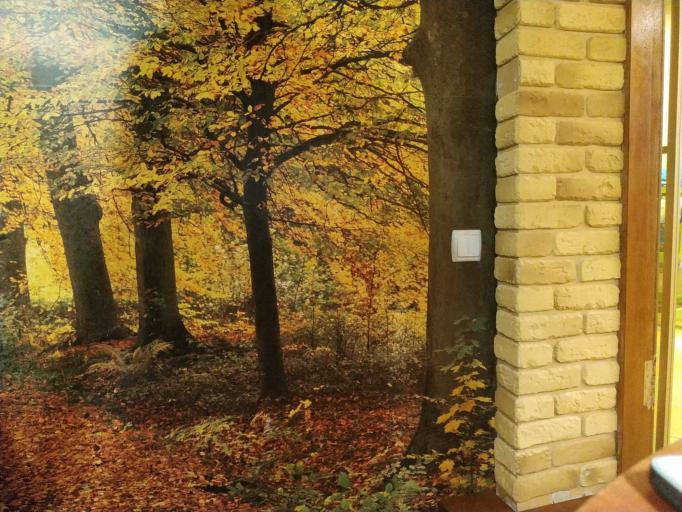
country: RU
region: Novgorod
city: Kulotino
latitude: 58.5362
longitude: 33.2797
